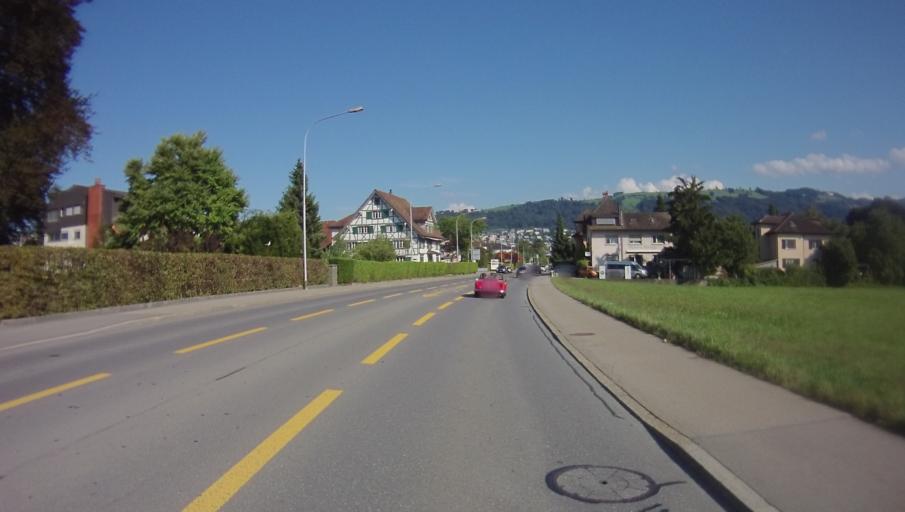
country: CH
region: Zug
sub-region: Zug
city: Steinhausen
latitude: 47.1781
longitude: 8.4961
